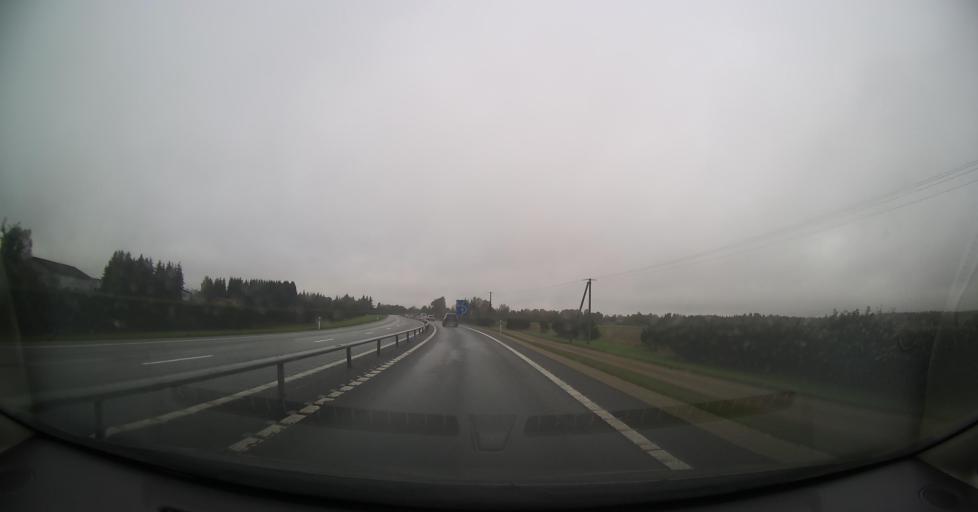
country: EE
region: Jogevamaa
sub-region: Jogeva linn
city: Jogeva
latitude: 58.6030
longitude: 26.2299
